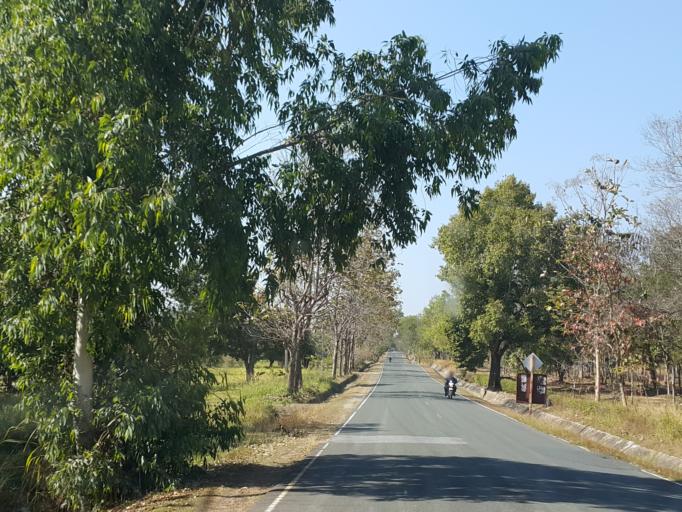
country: TH
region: Chiang Mai
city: Chiang Mai
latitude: 18.8585
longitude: 98.9512
